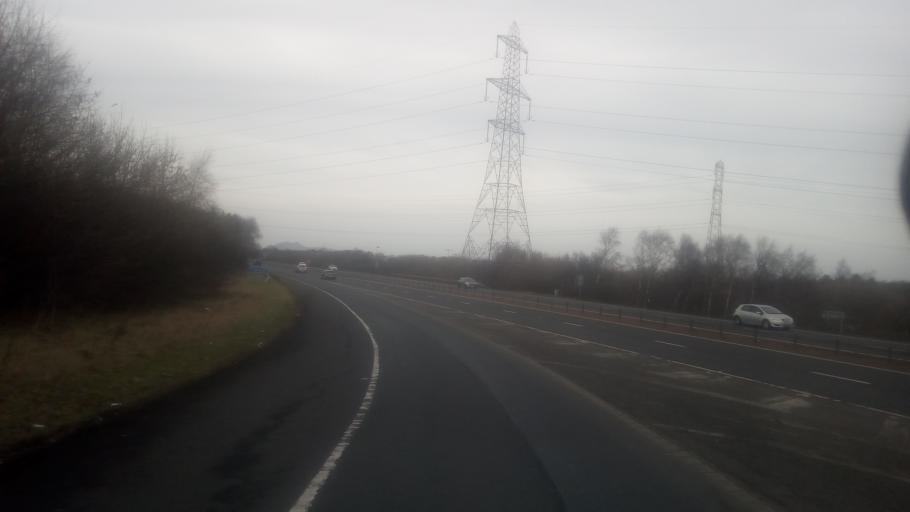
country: GB
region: Scotland
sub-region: East Lothian
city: Tranent
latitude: 55.9519
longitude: -2.9567
